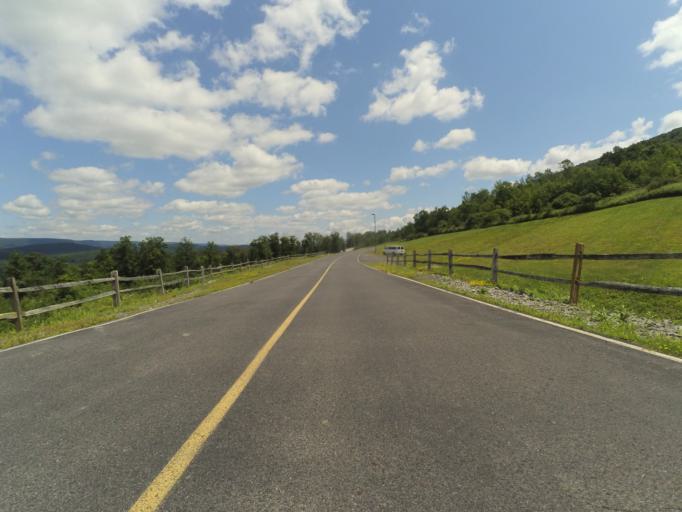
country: US
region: Pennsylvania
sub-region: Centre County
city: Stormstown
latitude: 40.8274
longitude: -77.9993
